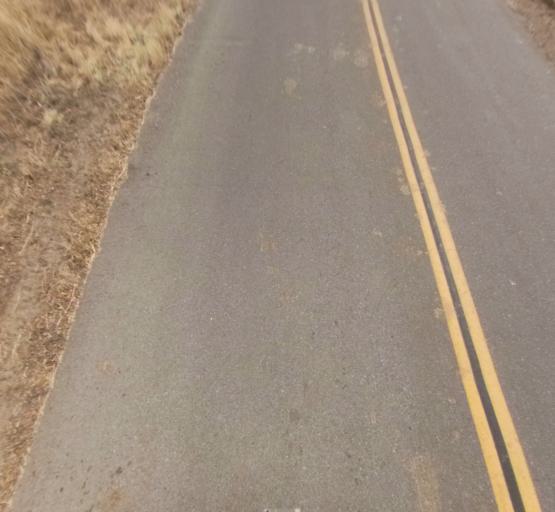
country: US
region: California
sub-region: Madera County
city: Yosemite Lakes
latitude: 37.1117
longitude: -119.6620
